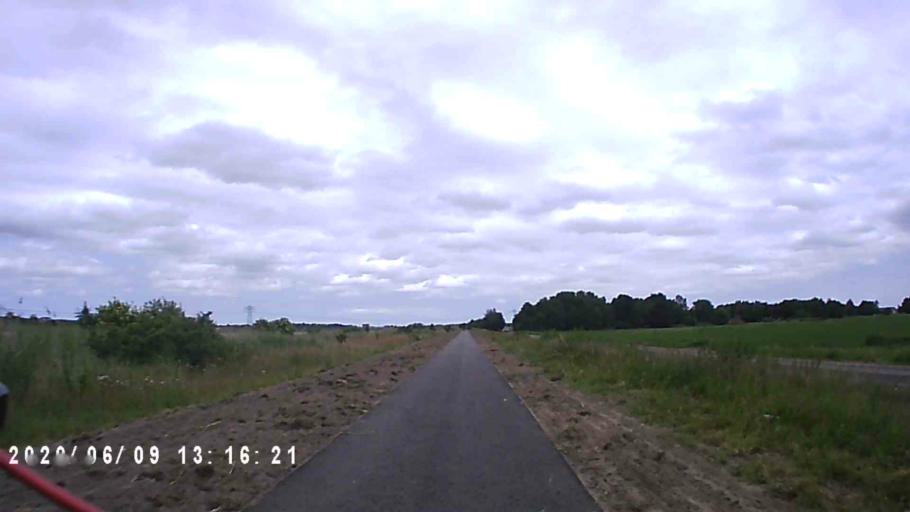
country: NL
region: Groningen
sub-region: Gemeente Haren
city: Haren
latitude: 53.2193
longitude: 6.6704
